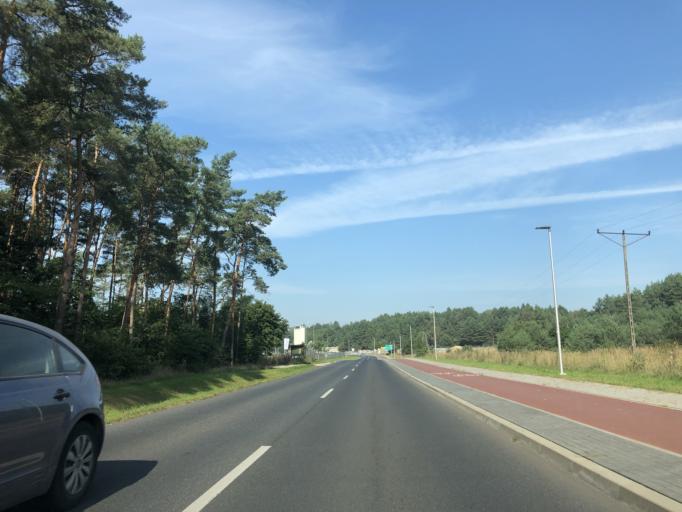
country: PL
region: Greater Poland Voivodeship
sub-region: Powiat pilski
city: Pila
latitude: 53.1386
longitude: 16.7909
